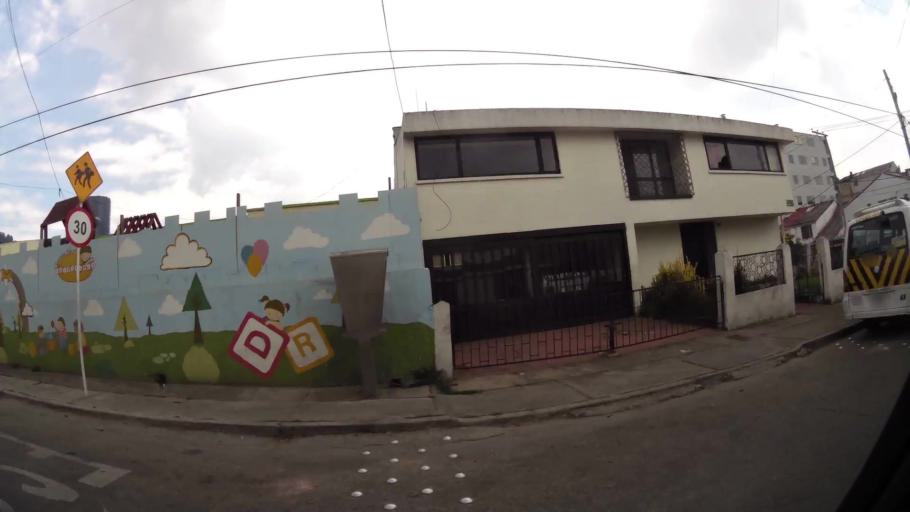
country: CO
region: Cundinamarca
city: La Calera
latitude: 4.7372
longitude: -74.0261
